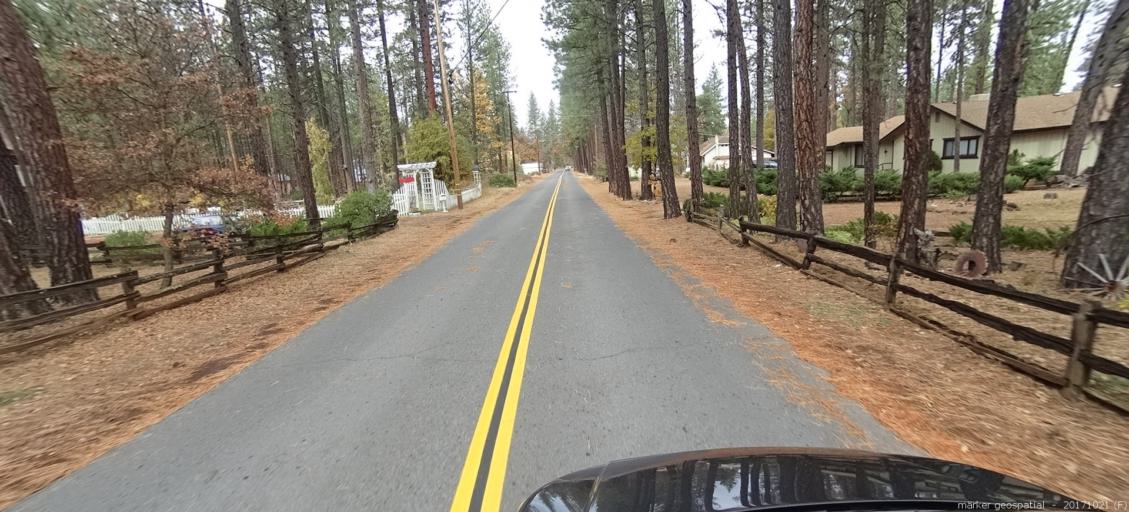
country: US
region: California
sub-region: Shasta County
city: Burney
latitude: 40.9982
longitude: -121.6312
